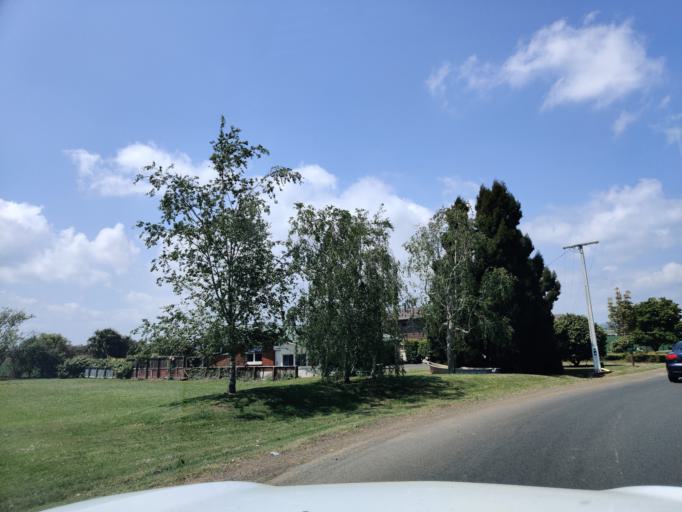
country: NZ
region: Auckland
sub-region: Auckland
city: Pukekohe East
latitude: -37.2396
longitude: 174.9509
